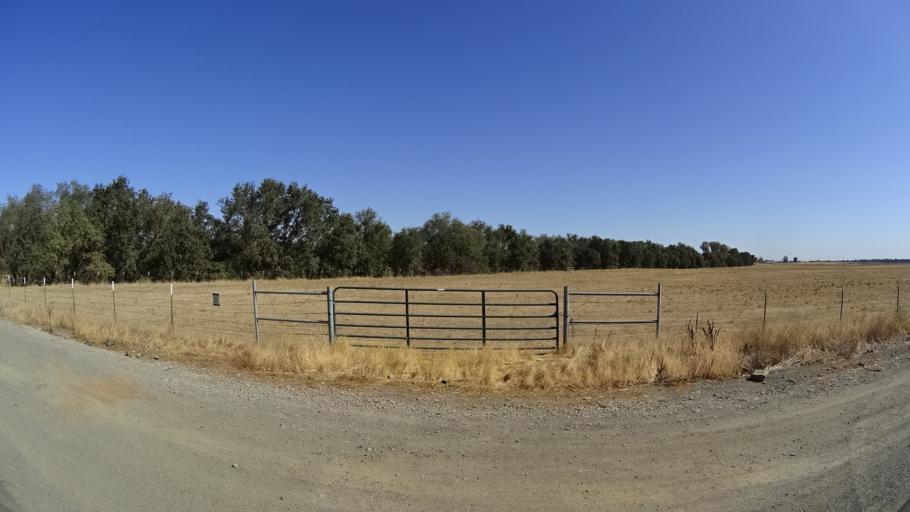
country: US
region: California
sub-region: Solano County
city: Dixon
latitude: 38.5451
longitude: -121.8550
